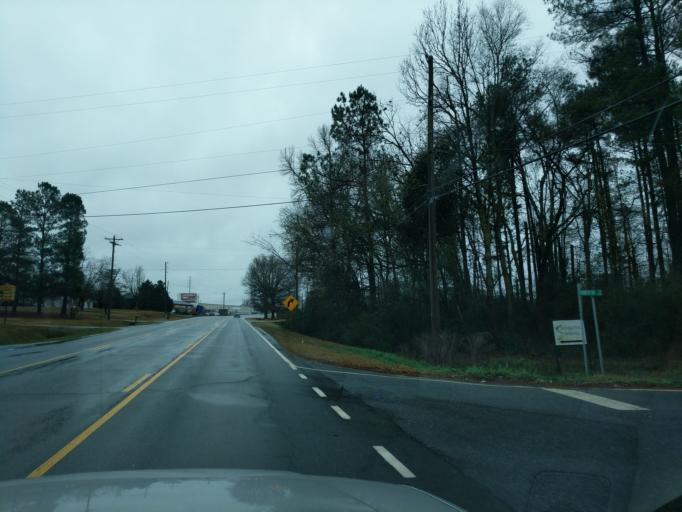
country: US
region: Georgia
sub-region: Franklin County
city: Lavonia
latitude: 34.4188
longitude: -83.1008
